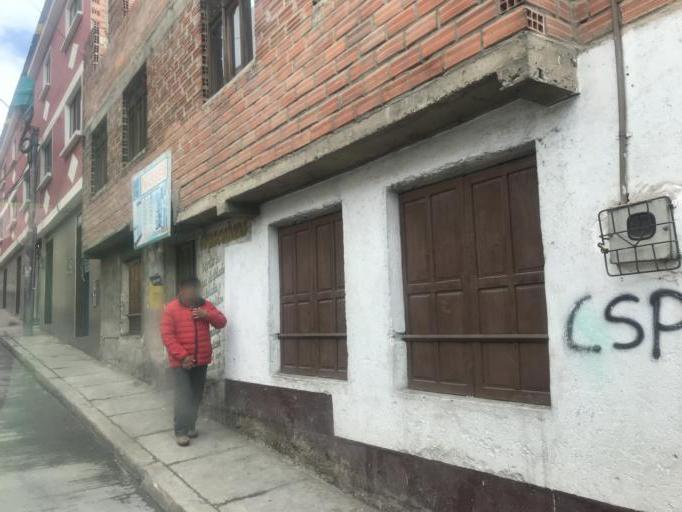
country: BO
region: Potosi
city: Potosi
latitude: -19.5952
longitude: -65.7497
